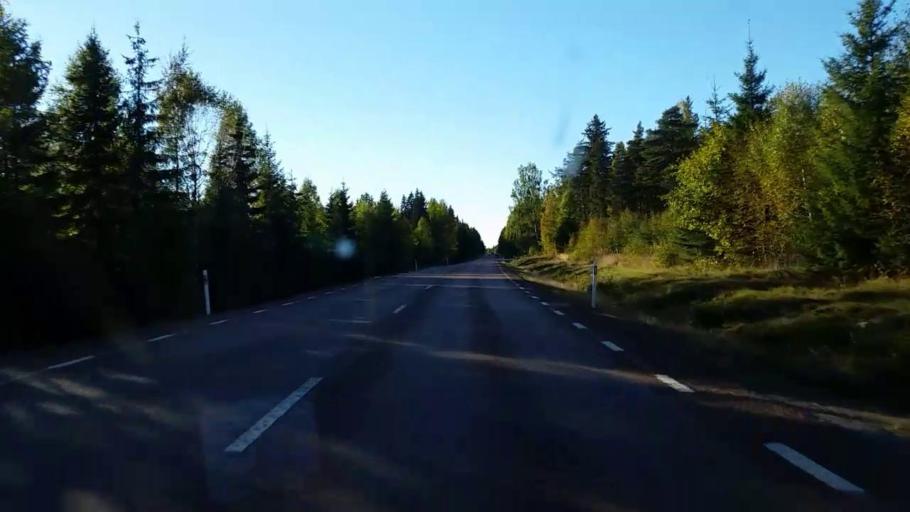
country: SE
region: Gaevleborg
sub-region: Ljusdals Kommun
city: Ljusdal
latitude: 61.8200
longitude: 16.1647
